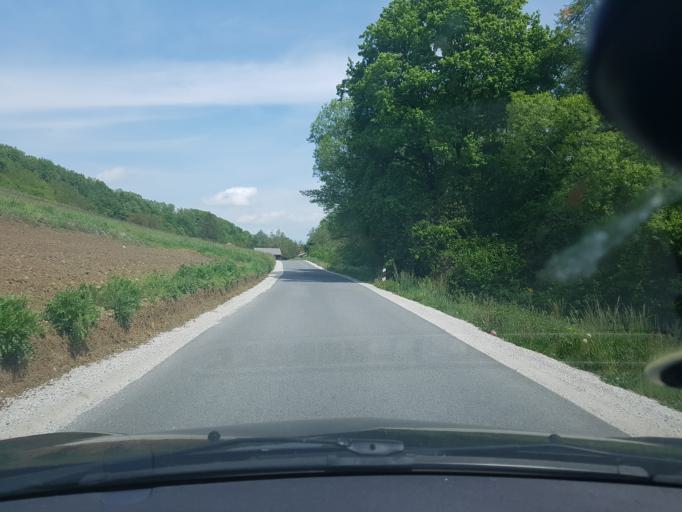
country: HR
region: Krapinsko-Zagorska
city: Pregrada
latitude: 46.1983
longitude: 15.7284
